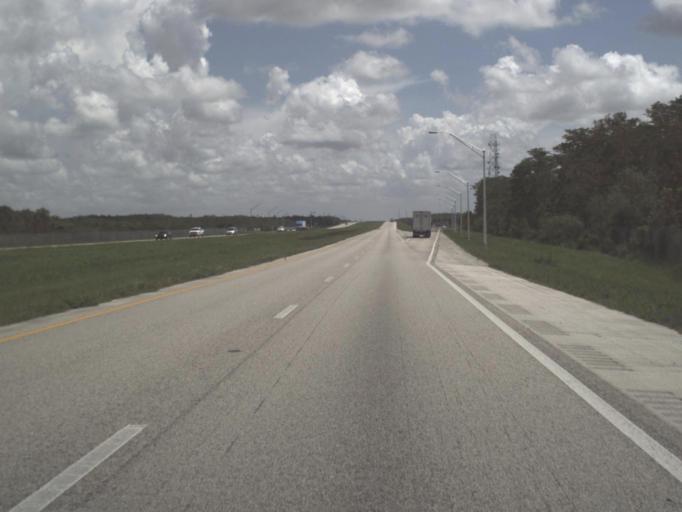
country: US
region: Florida
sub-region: Collier County
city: Immokalee
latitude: 26.1682
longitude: -81.0869
